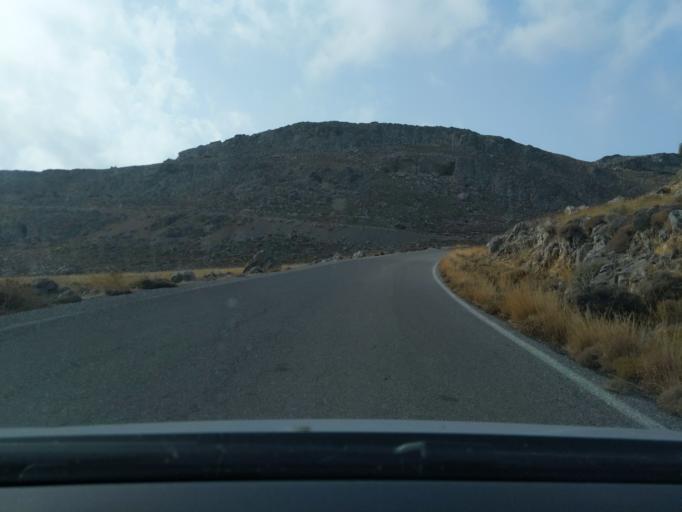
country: GR
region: Crete
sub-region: Nomos Lasithiou
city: Palekastro
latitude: 35.0925
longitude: 26.2634
